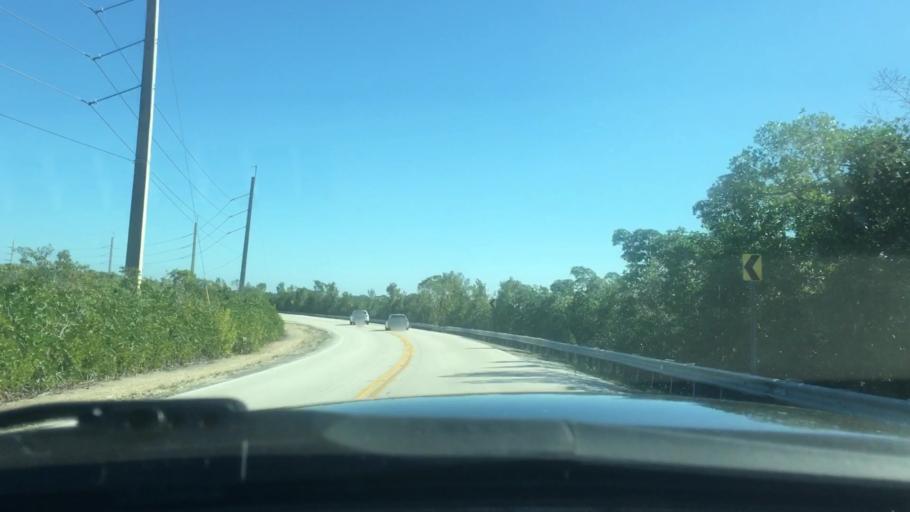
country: US
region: Florida
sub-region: Monroe County
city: North Key Largo
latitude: 25.2791
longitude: -80.3413
